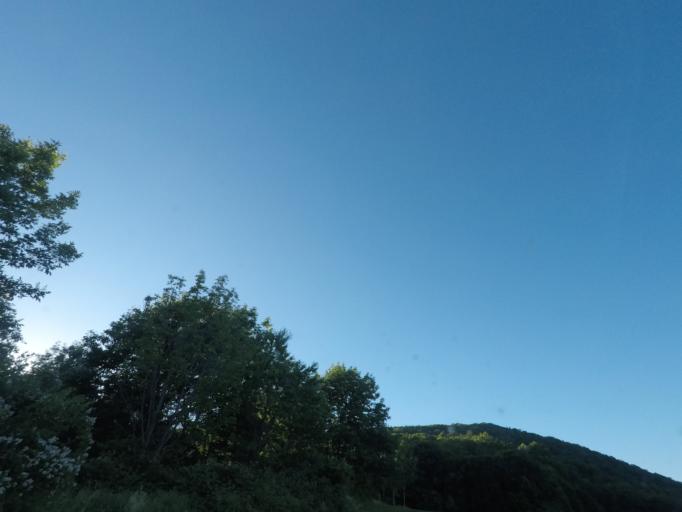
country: US
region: Massachusetts
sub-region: Berkshire County
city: Lenox
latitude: 42.3534
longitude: -73.3137
